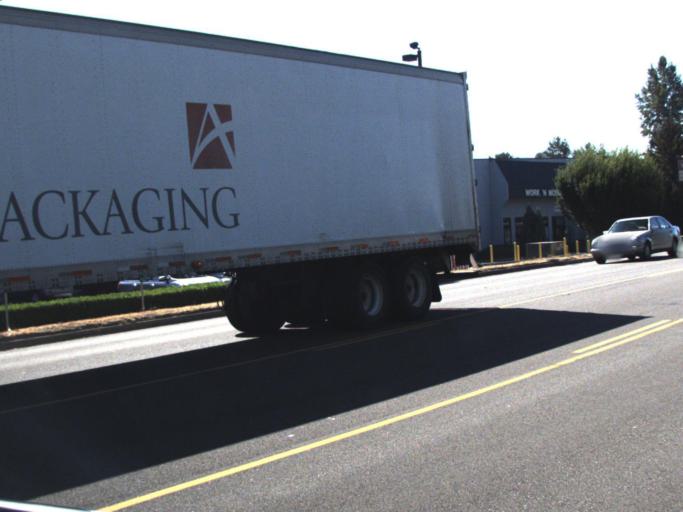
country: US
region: Washington
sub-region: King County
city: Tukwila
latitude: 47.4437
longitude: -122.2459
